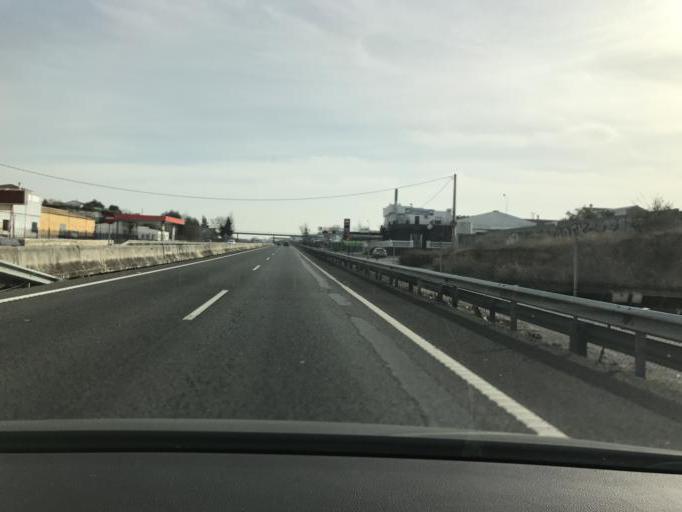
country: ES
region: Andalusia
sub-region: Provincia de Granada
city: Moraleda de Zafayona
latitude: 37.1862
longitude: -3.9607
